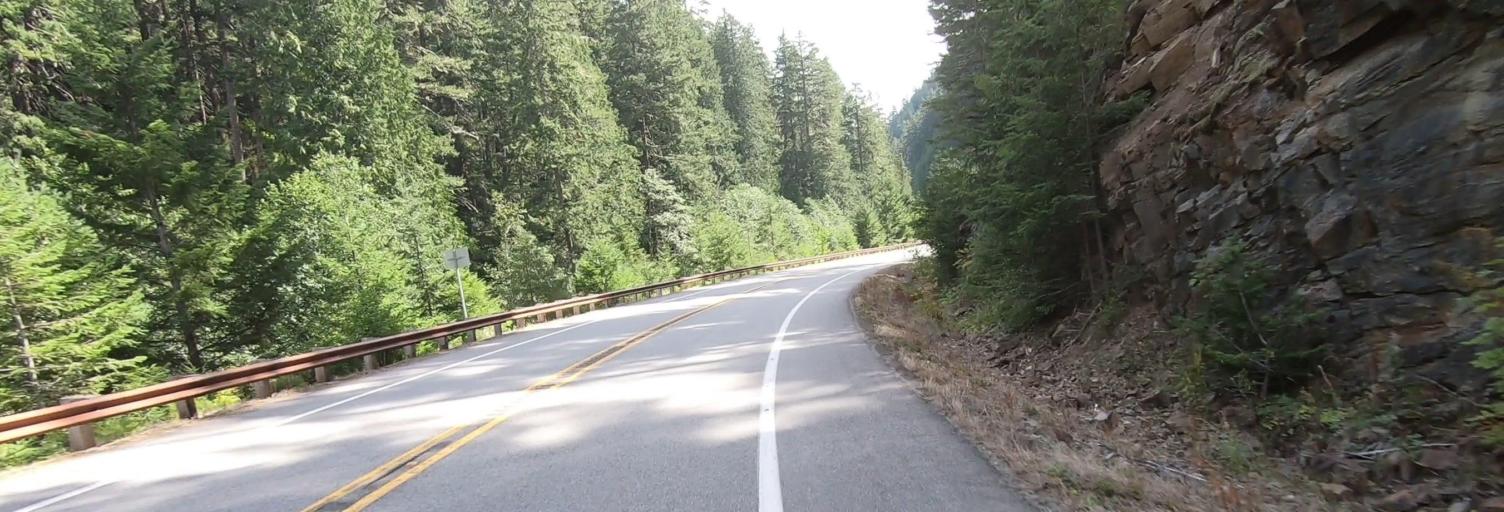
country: US
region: Washington
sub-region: Snohomish County
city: Darrington
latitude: 48.6872
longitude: -120.9126
